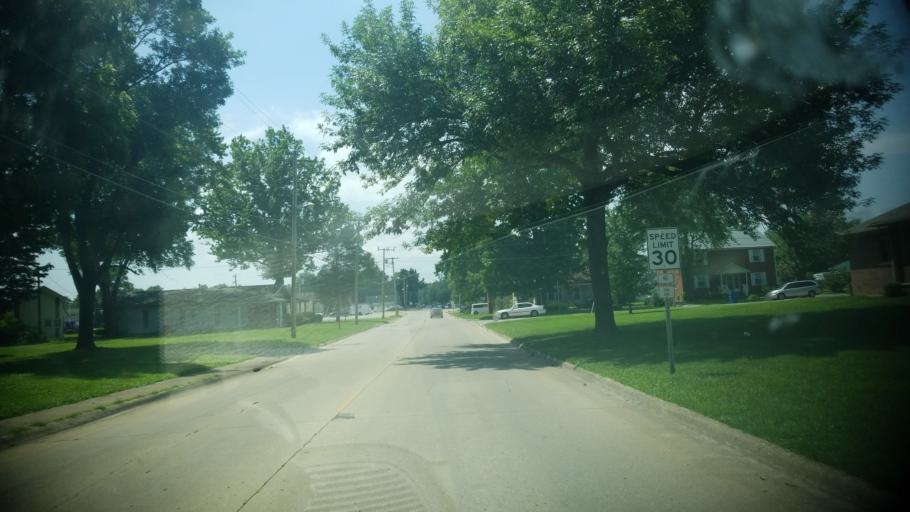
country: US
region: Illinois
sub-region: Wayne County
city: Fairfield
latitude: 38.3810
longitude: -88.3538
